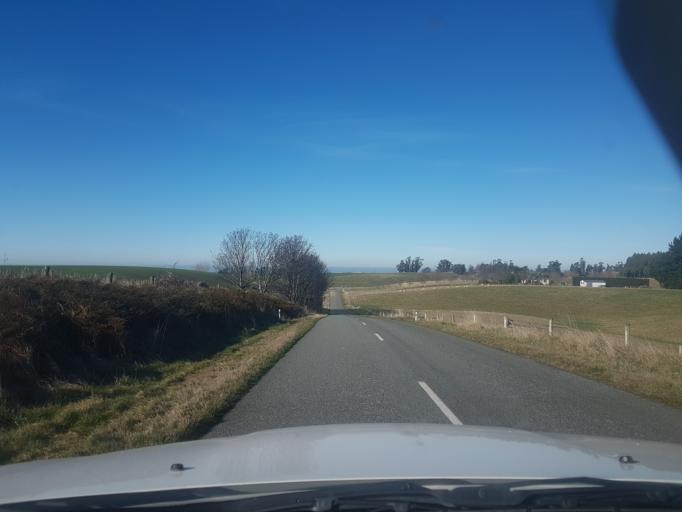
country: NZ
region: Canterbury
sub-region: Timaru District
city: Pleasant Point
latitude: -44.3768
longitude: 171.0838
